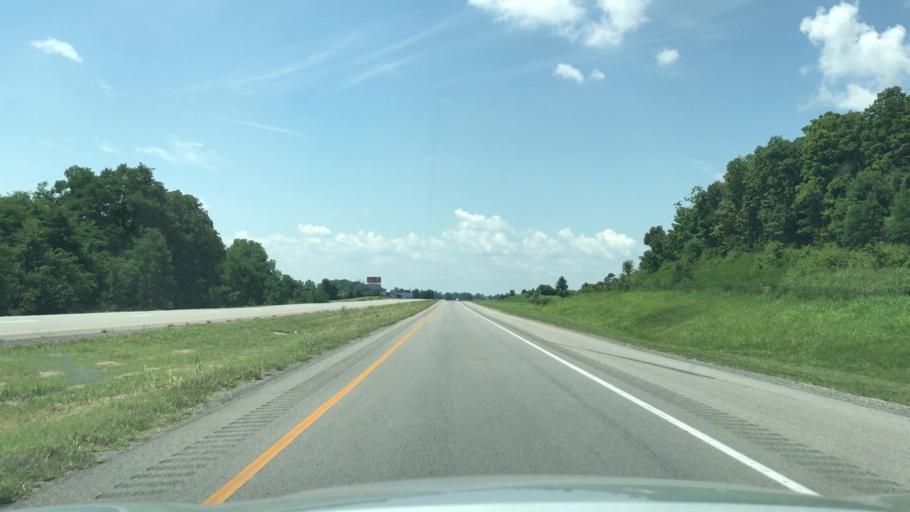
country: US
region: Kentucky
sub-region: Clinton County
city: Albany
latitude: 36.7282
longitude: -85.1357
